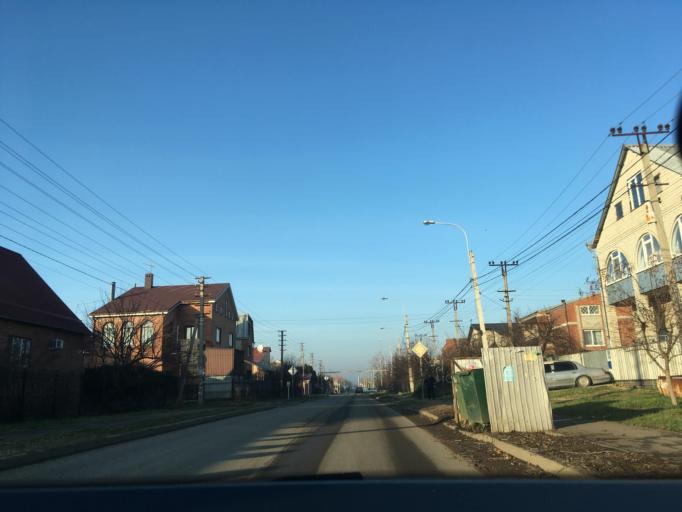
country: RU
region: Krasnodarskiy
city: Krasnodar
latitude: 45.1161
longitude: 39.0147
